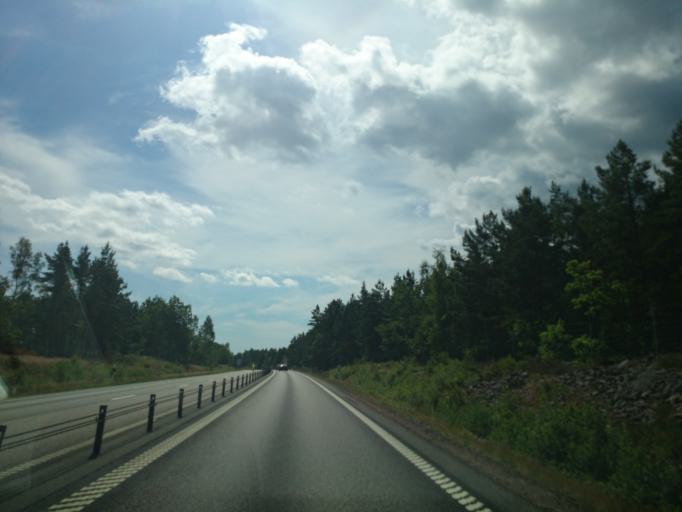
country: SE
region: Kalmar
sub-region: Oskarshamns Kommun
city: Paskallavik
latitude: 57.1370
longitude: 16.4717
